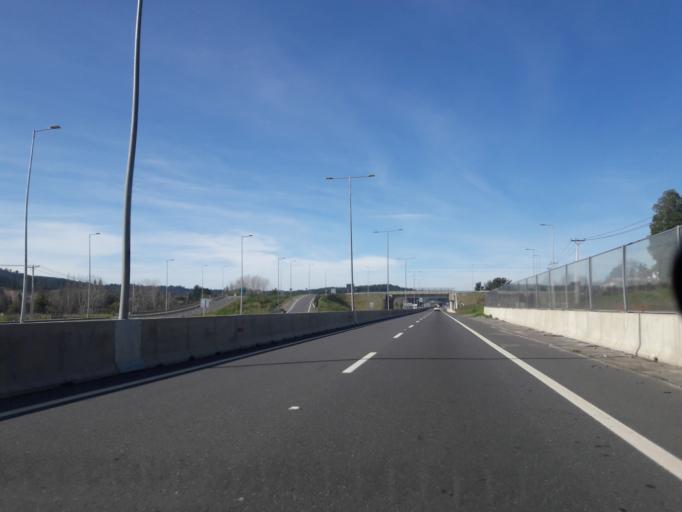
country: CL
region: Biobio
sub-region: Provincia de Biobio
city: Yumbel
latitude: -36.9865
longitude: -72.6215
